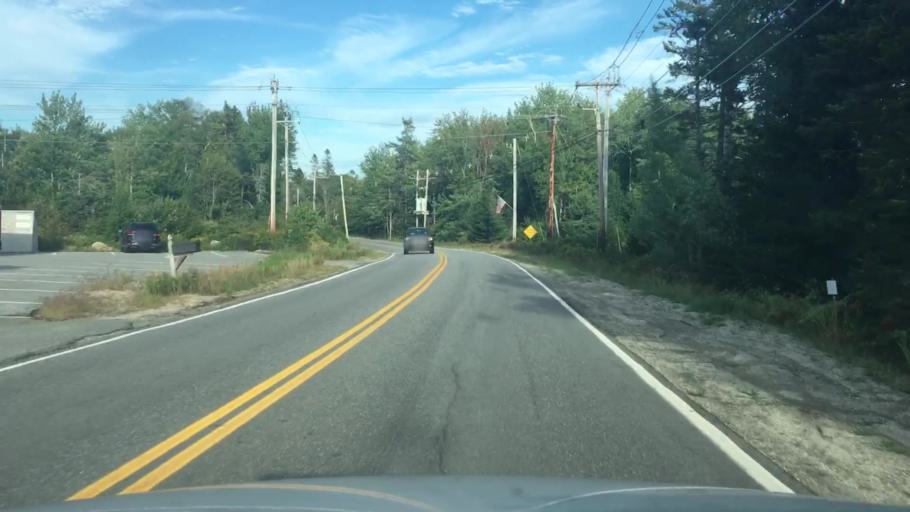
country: US
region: Maine
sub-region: Hancock County
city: Trenton
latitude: 44.4375
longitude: -68.3744
